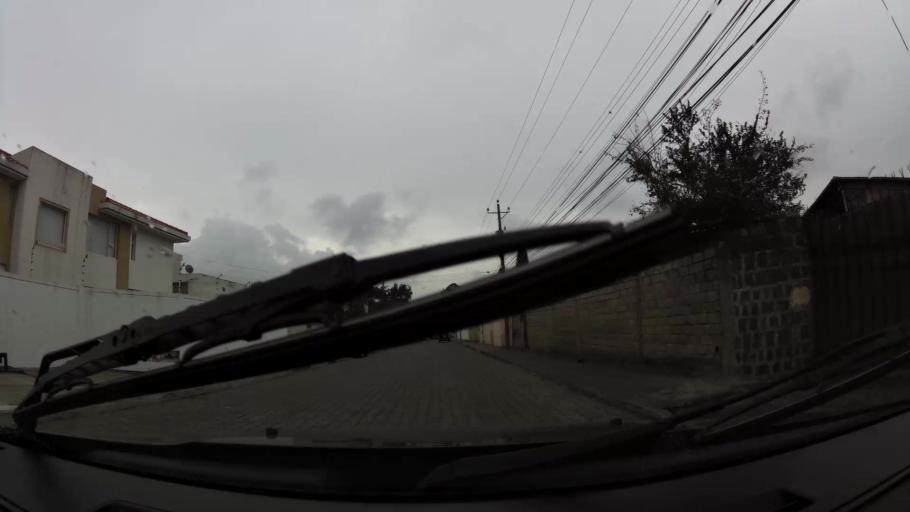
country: EC
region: Pichincha
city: Sangolqui
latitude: -0.2800
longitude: -78.4676
